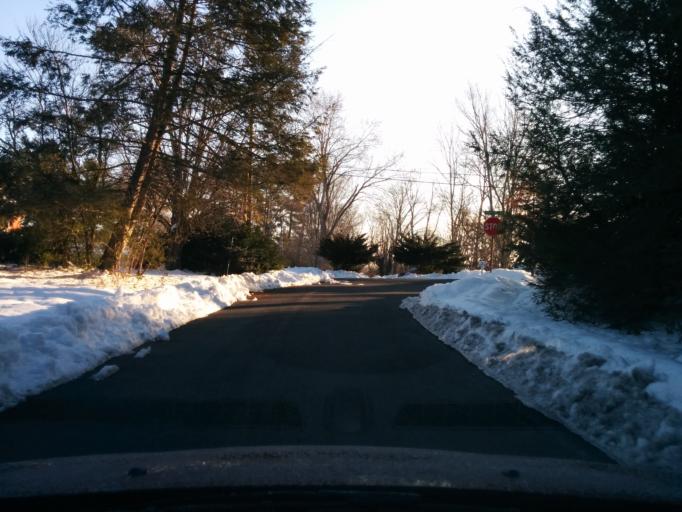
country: US
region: Virginia
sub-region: City of Lexington
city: Lexington
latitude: 37.7751
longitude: -79.4543
